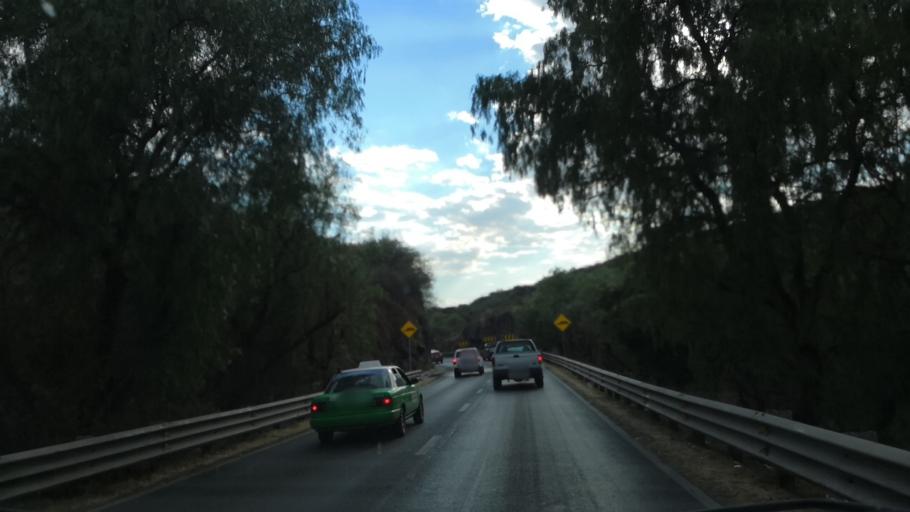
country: MX
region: Guanajuato
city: Marfil
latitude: 21.0080
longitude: -101.2734
